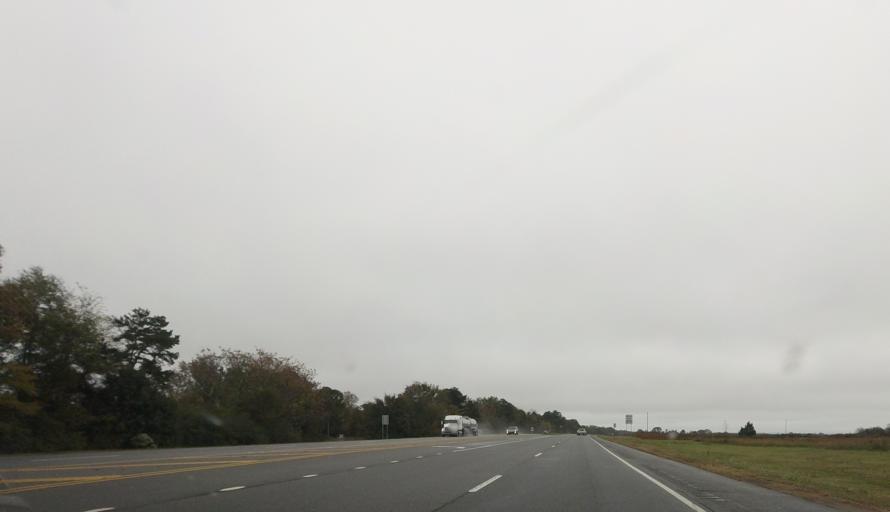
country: US
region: Georgia
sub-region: Taylor County
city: Reynolds
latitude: 32.5591
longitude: -84.0815
